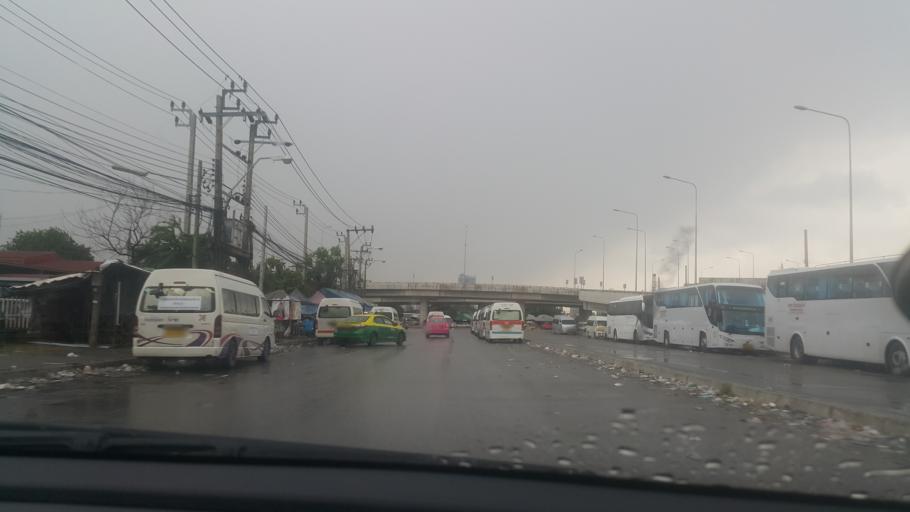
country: TH
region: Bangkok
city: Bang Sue
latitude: 13.8126
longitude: 100.5459
